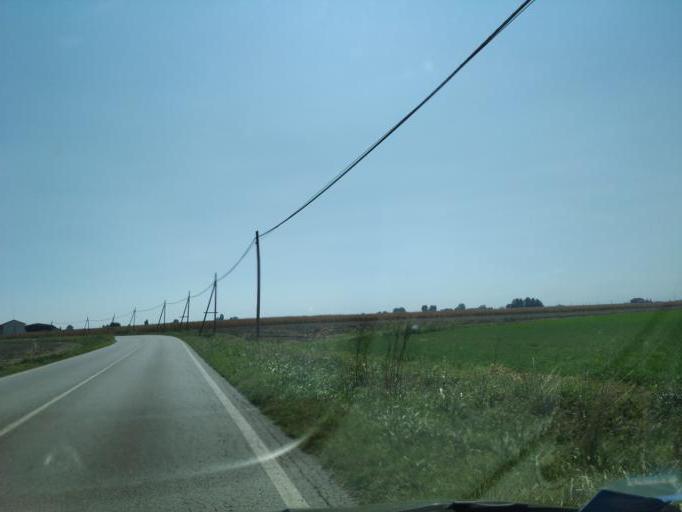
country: IT
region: Emilia-Romagna
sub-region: Provincia di Ferrara
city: Coccanile-Cesta
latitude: 44.8846
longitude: 11.8628
